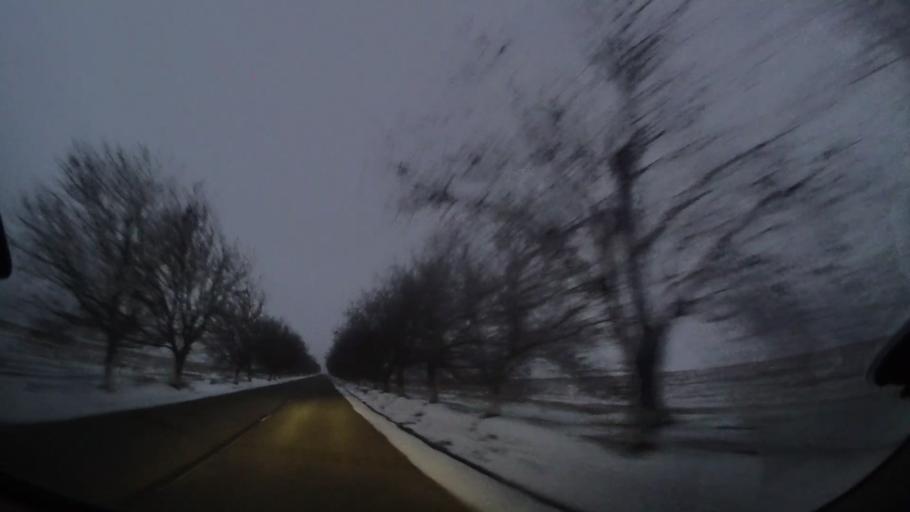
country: RO
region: Vaslui
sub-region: Comuna Dimitrie Cantemir
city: Dimitrie Cantemir
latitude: 46.5190
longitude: 28.0281
